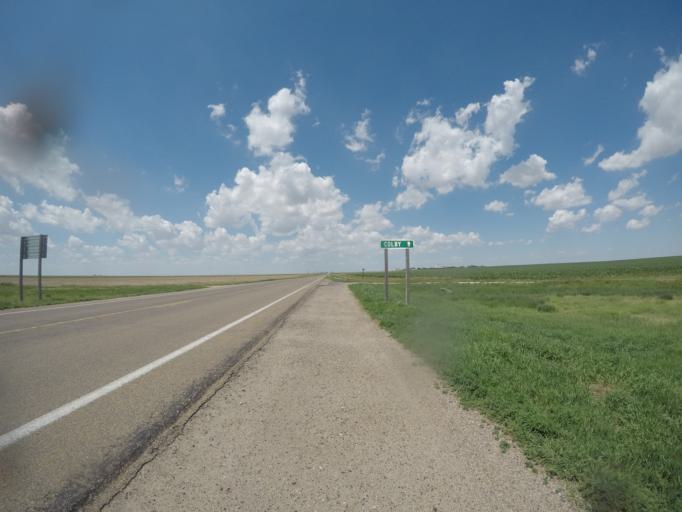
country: US
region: Kansas
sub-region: Thomas County
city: Colby
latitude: 39.3674
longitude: -101.2042
